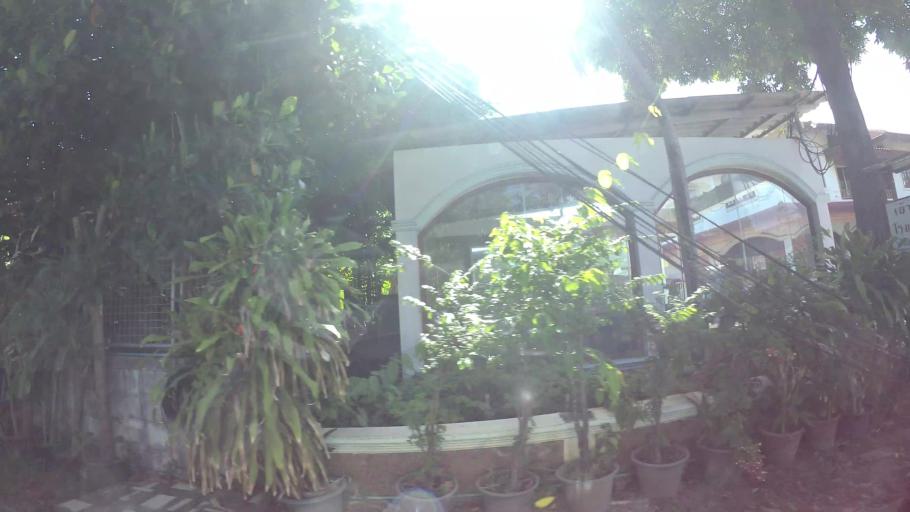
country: TH
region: Rayong
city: Rayong
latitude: 12.6744
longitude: 101.2918
